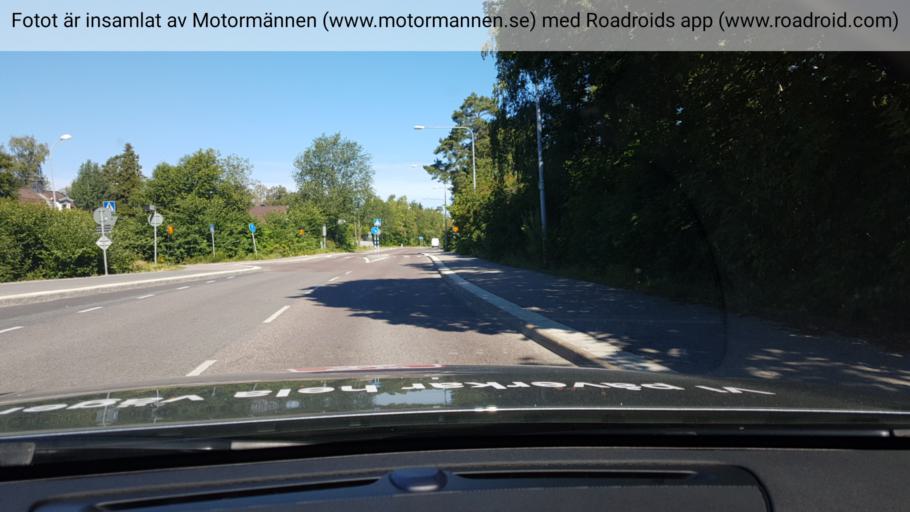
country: SE
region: Stockholm
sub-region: Huddinge Kommun
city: Huddinge
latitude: 59.2554
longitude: 17.9828
